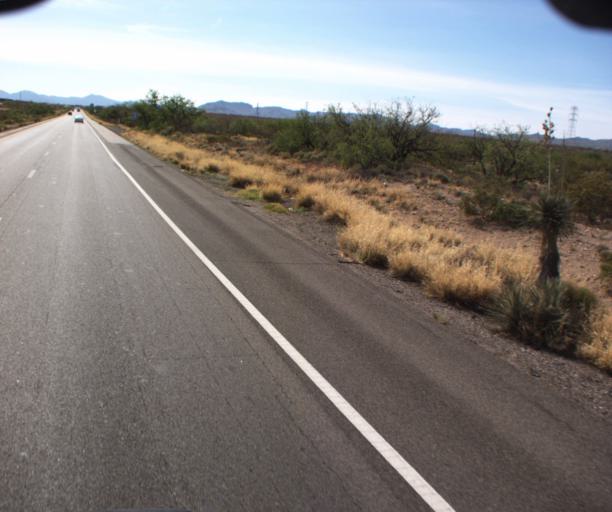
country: US
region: Arizona
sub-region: Pima County
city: Vail
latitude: 32.0228
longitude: -110.7142
